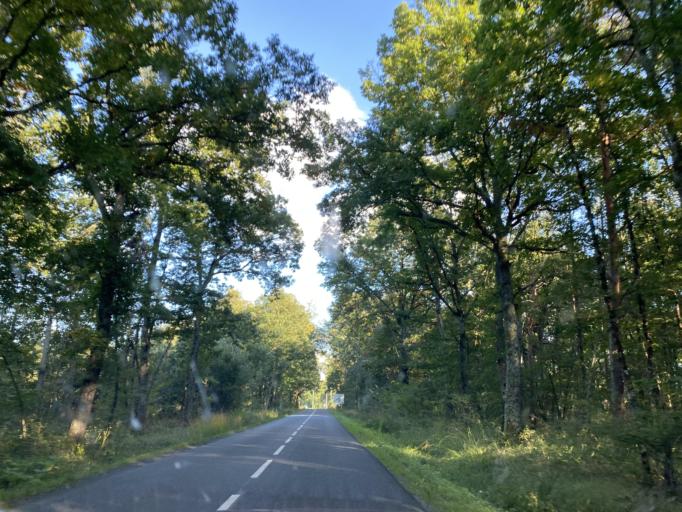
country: FR
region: Auvergne
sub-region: Departement du Puy-de-Dome
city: Randan
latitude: 46.0271
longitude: 3.3509
